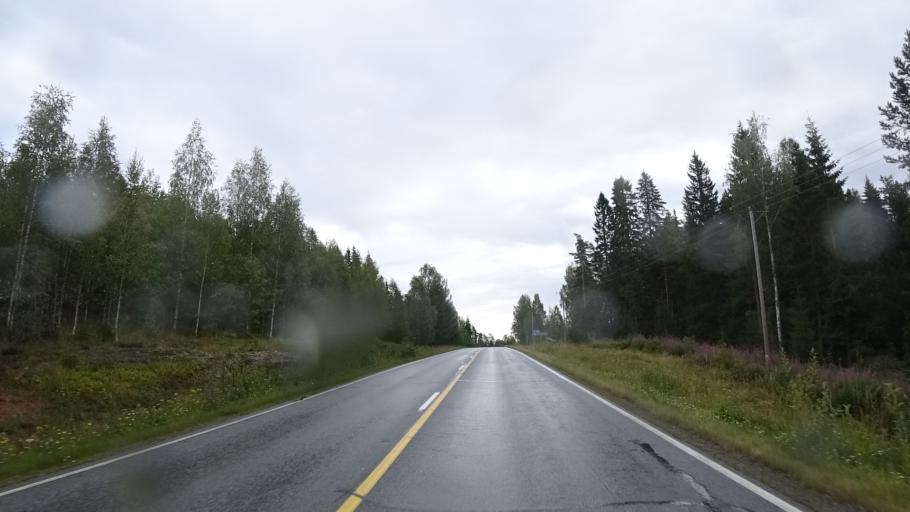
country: FI
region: North Karelia
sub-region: Keski-Karjala
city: Kesaelahti
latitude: 62.1060
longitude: 29.8237
